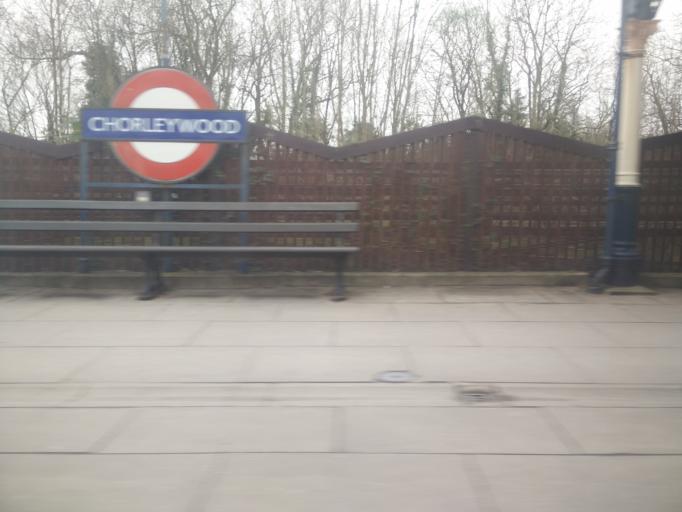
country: GB
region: England
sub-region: Hertfordshire
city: Chorleywood
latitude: 51.6541
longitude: -0.5183
